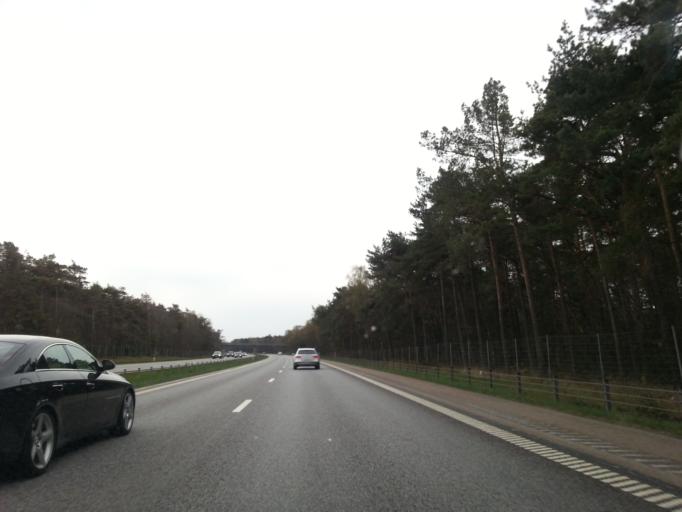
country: SE
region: Halland
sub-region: Halmstads Kommun
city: Paarp
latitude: 56.5706
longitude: 12.9492
